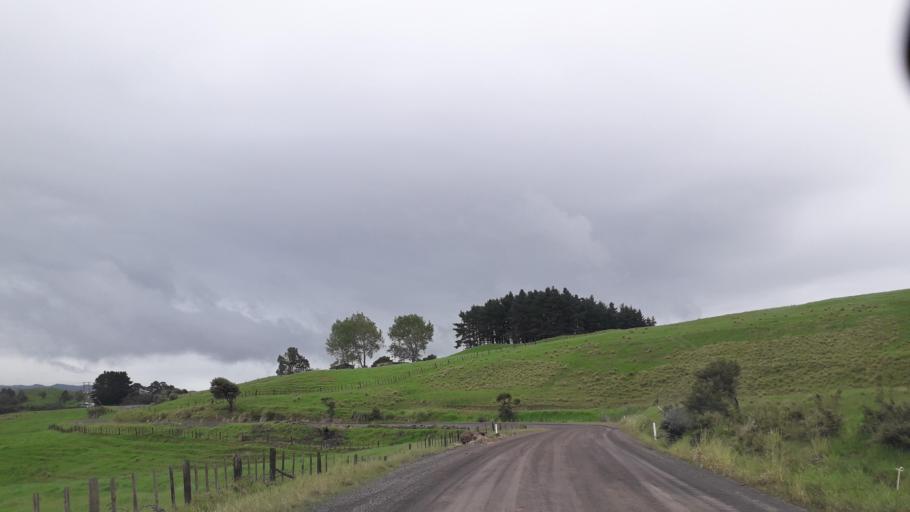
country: NZ
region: Northland
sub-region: Far North District
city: Kaitaia
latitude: -35.4084
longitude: 173.3639
